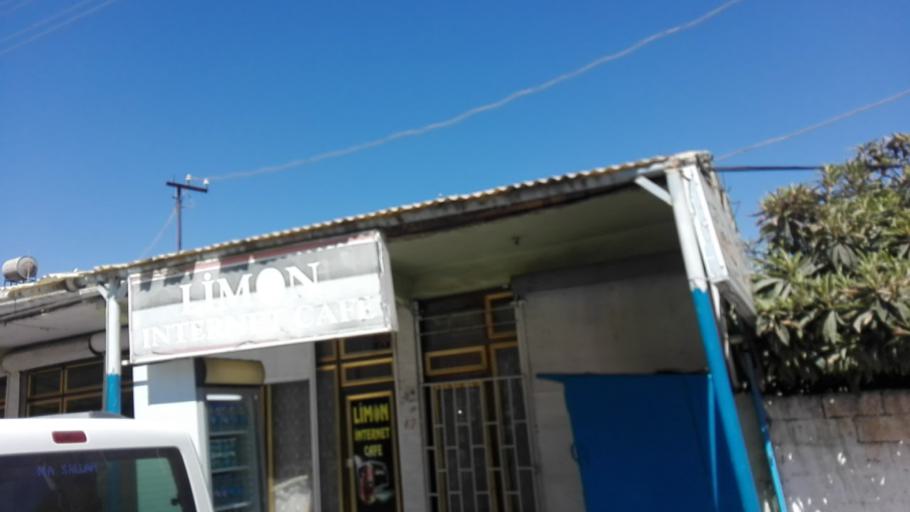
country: TR
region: Batman
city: Hasankeyf
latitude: 37.7129
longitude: 41.4150
